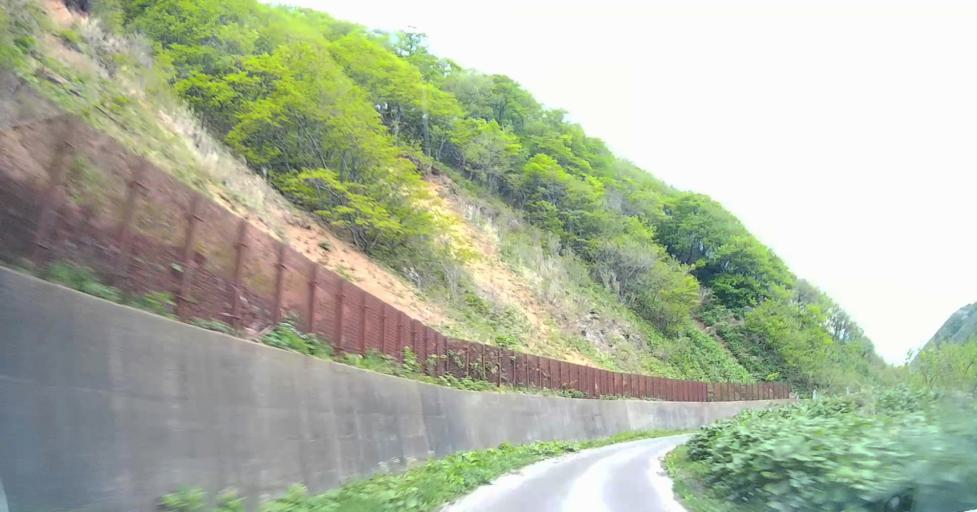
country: JP
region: Aomori
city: Shimokizukuri
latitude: 41.2382
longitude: 140.3443
